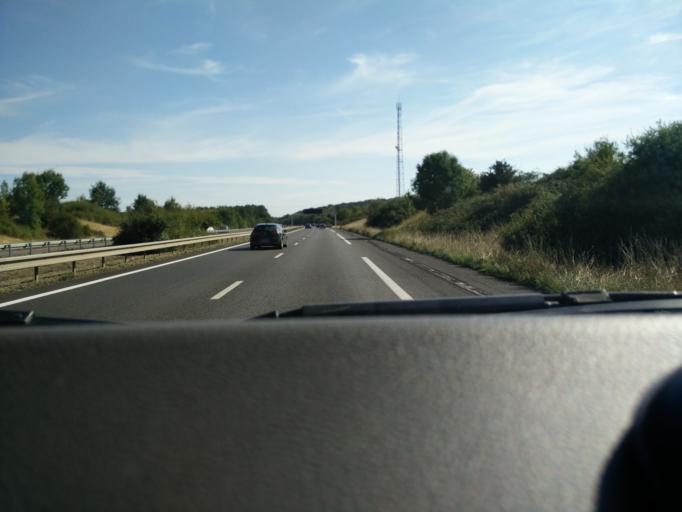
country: FR
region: Lorraine
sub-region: Departement de la Moselle
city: Corny-sur-Moselle
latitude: 48.9789
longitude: 6.1041
